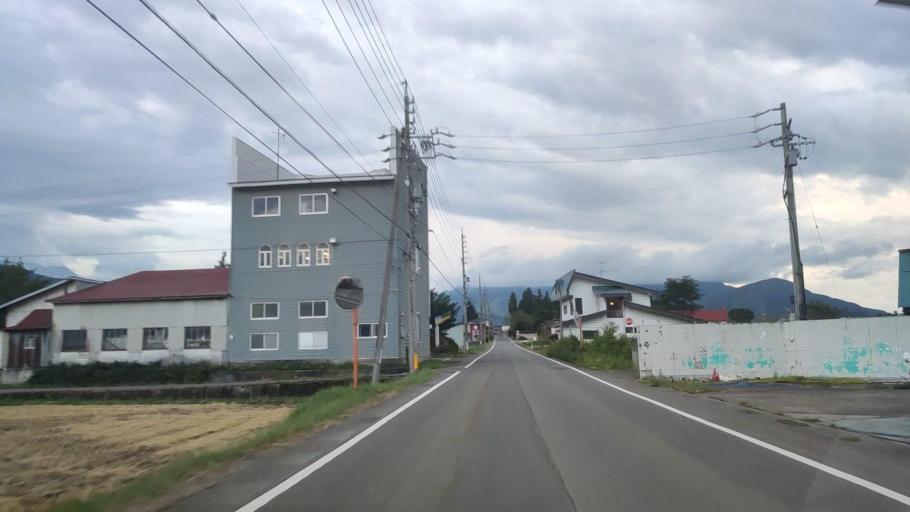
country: JP
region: Nagano
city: Iiyama
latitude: 36.8713
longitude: 138.4076
